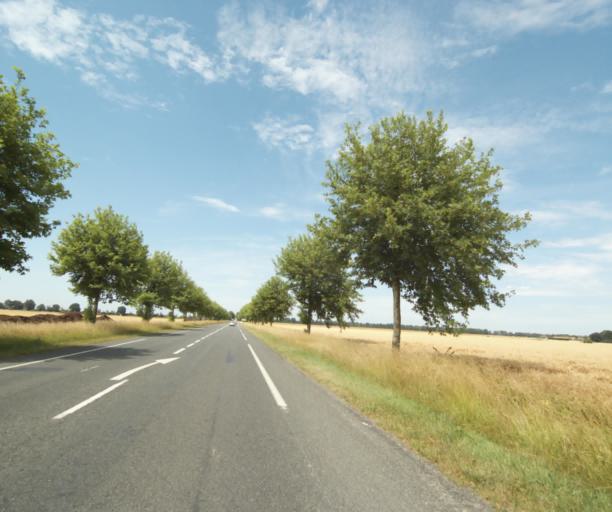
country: FR
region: Ile-de-France
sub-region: Departement de Seine-et-Marne
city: Chailly-en-Biere
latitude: 48.4838
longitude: 2.5927
